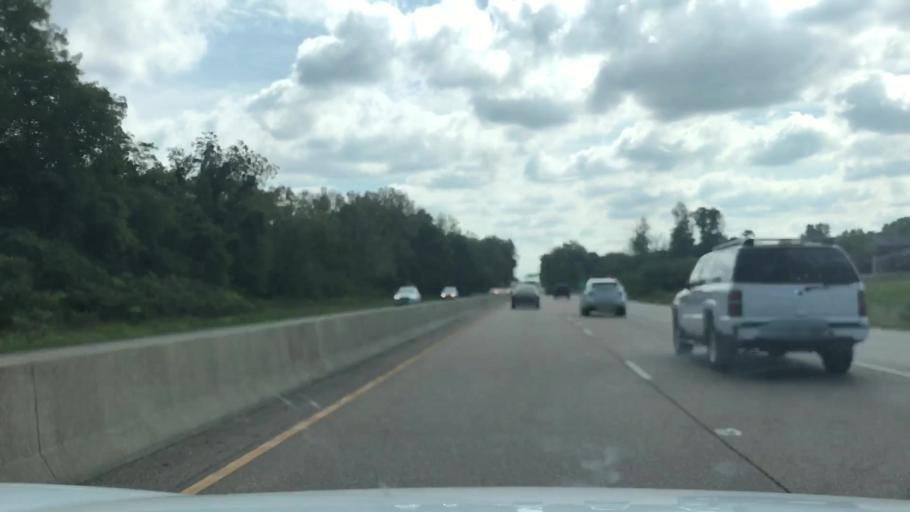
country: US
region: Illinois
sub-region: Saint Clair County
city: Alorton
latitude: 38.5553
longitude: -90.0773
